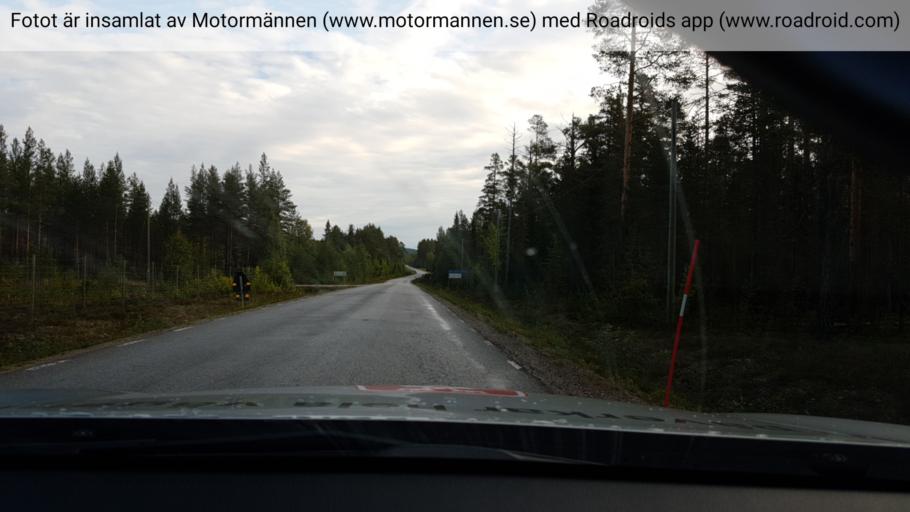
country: SE
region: Vaesterbotten
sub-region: Vindelns Kommun
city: Vindeln
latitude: 64.2314
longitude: 19.7850
